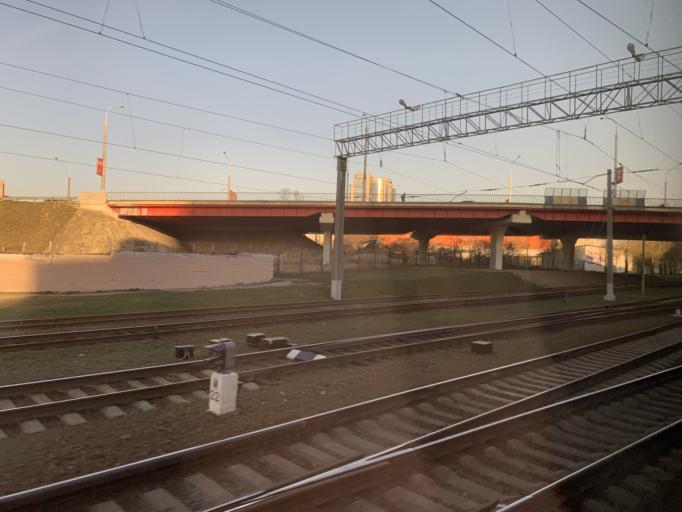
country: BY
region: Minsk
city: Minsk
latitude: 53.9099
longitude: 27.5233
